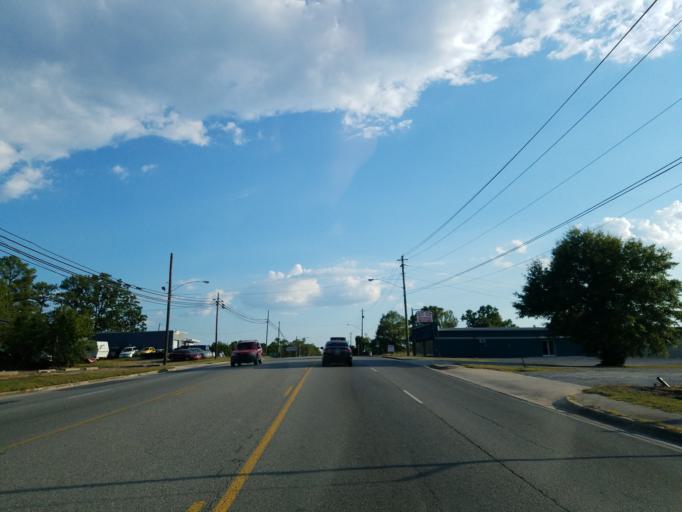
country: US
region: Georgia
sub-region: Murray County
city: Chatsworth
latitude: 34.7770
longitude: -84.7697
